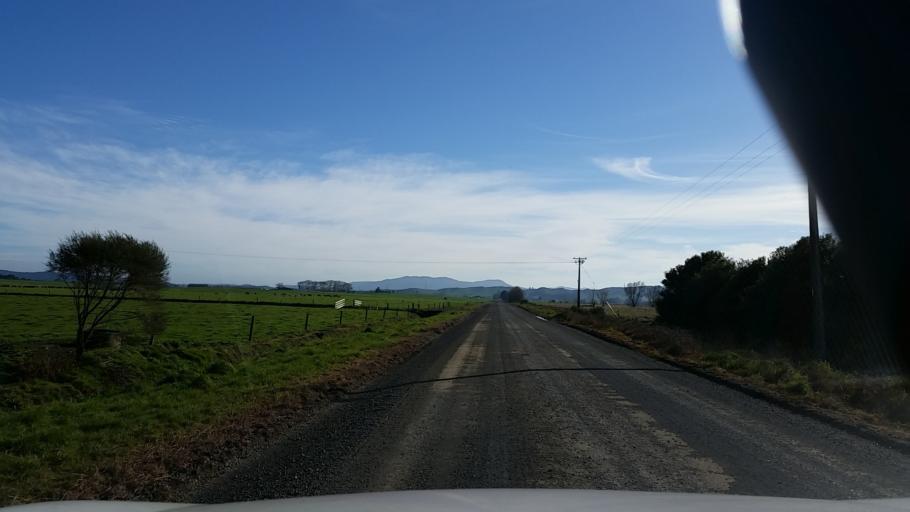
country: NZ
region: Waikato
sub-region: Hamilton City
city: Hamilton
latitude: -37.6342
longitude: 175.4291
